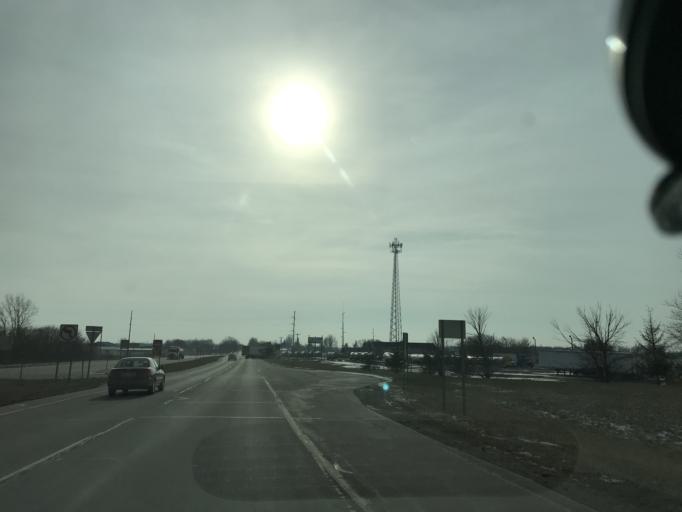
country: US
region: Michigan
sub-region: Ionia County
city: Ionia
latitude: 42.8771
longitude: -85.0751
